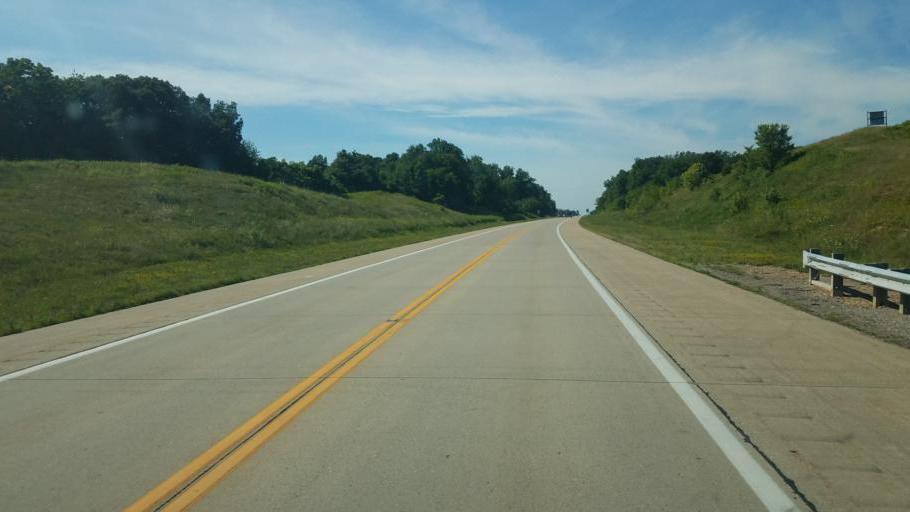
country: US
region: Ohio
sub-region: Meigs County
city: Pomeroy
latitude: 39.1556
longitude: -82.0336
